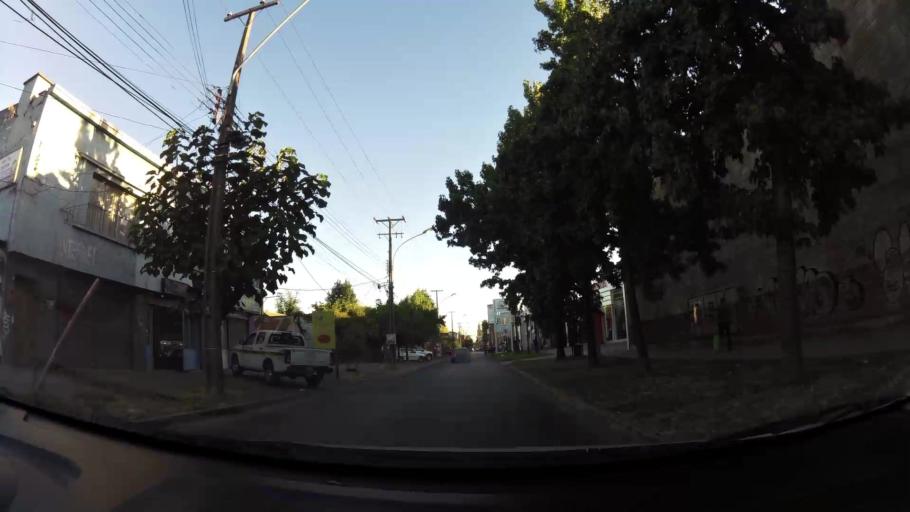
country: CL
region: Maule
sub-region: Provincia de Curico
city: Curico
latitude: -34.9790
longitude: -71.2410
